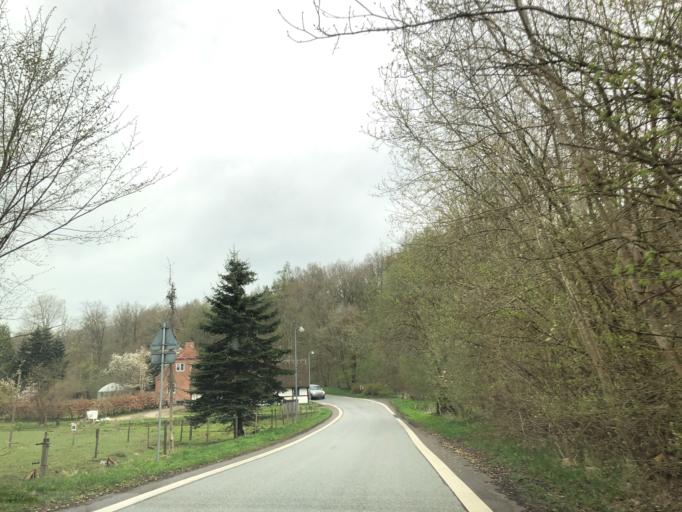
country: DK
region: Zealand
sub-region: Lejre Kommune
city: Kirke Hvalso
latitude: 55.5251
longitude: 11.8607
